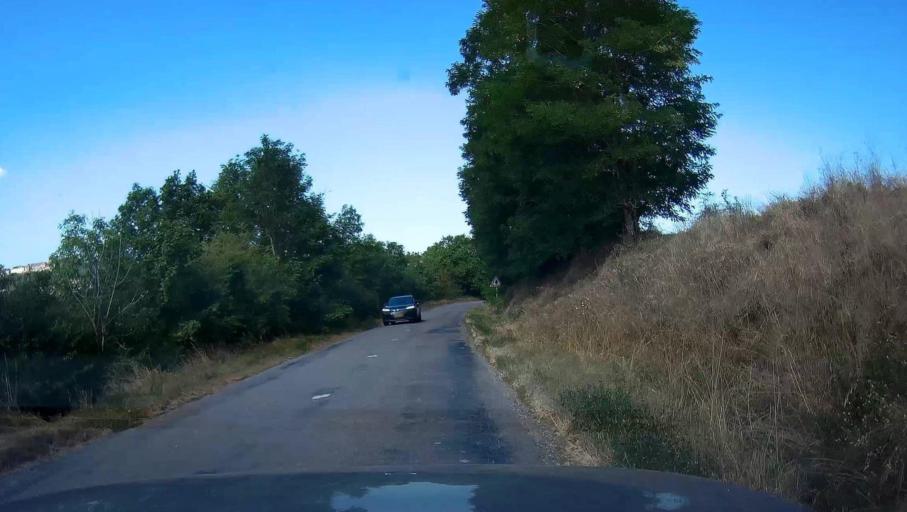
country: FR
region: Champagne-Ardenne
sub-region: Departement de la Haute-Marne
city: Langres
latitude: 47.8738
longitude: 5.3585
